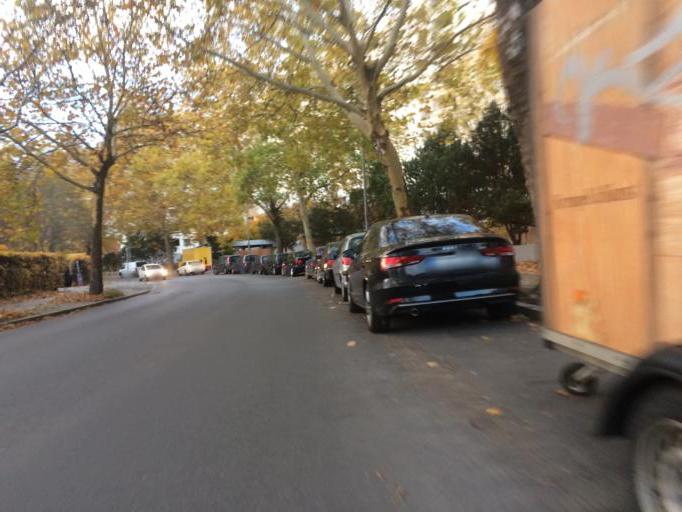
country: DE
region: Berlin
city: Markisches Viertel
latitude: 52.6049
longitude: 13.3615
